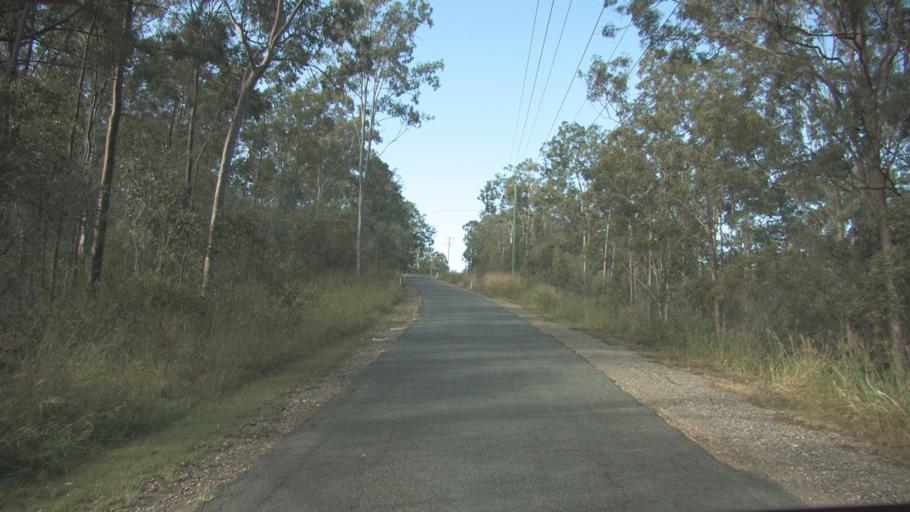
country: AU
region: Queensland
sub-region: Logan
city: Cedar Vale
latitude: -27.8251
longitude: 153.0689
